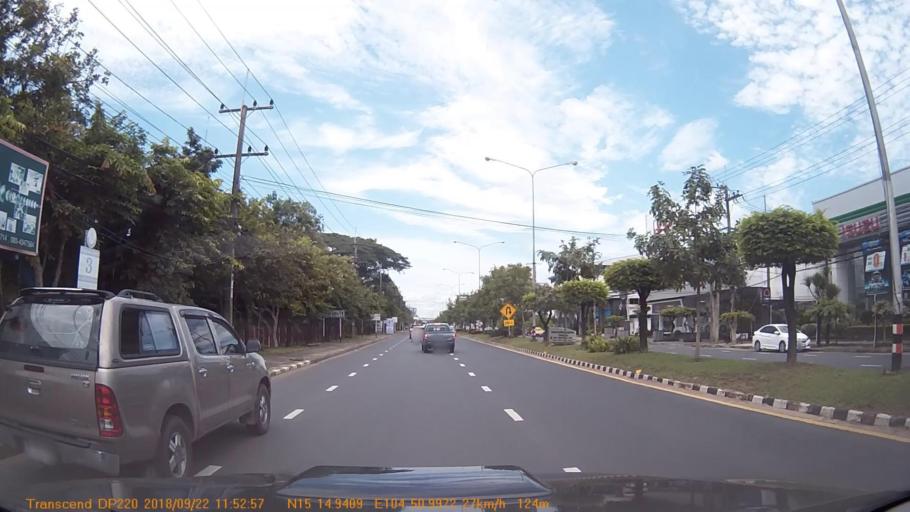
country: TH
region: Changwat Ubon Ratchathani
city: Ubon Ratchathani
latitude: 15.2490
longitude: 104.8500
